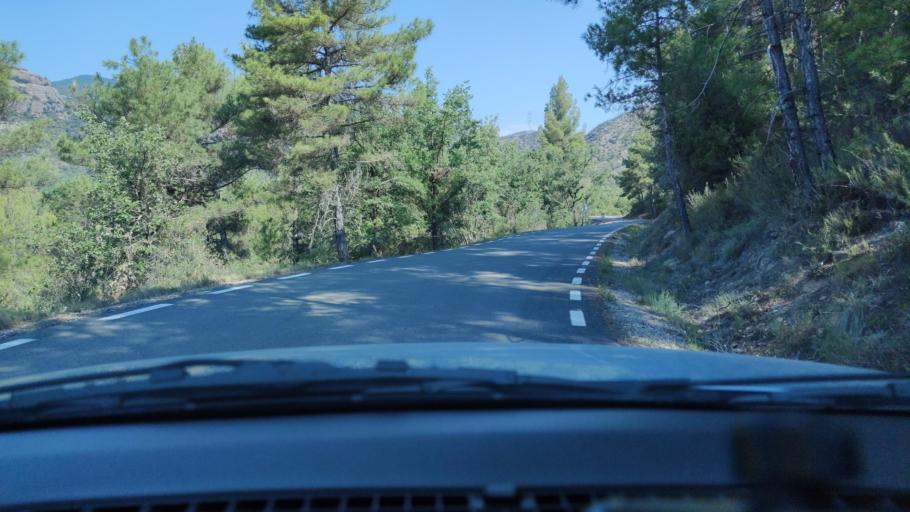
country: ES
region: Catalonia
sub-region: Provincia de Lleida
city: Senterada
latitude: 42.2787
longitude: 0.9427
